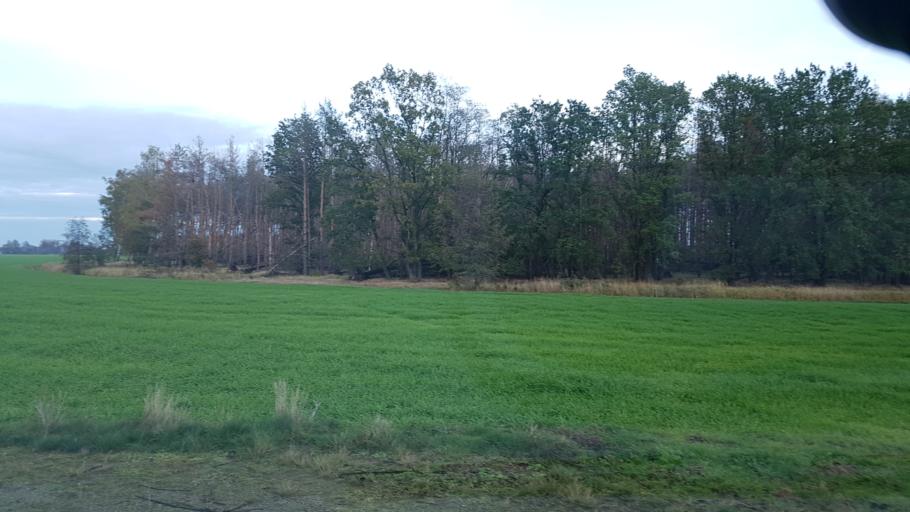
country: DE
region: Brandenburg
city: Falkenberg
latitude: 51.5348
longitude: 13.2675
